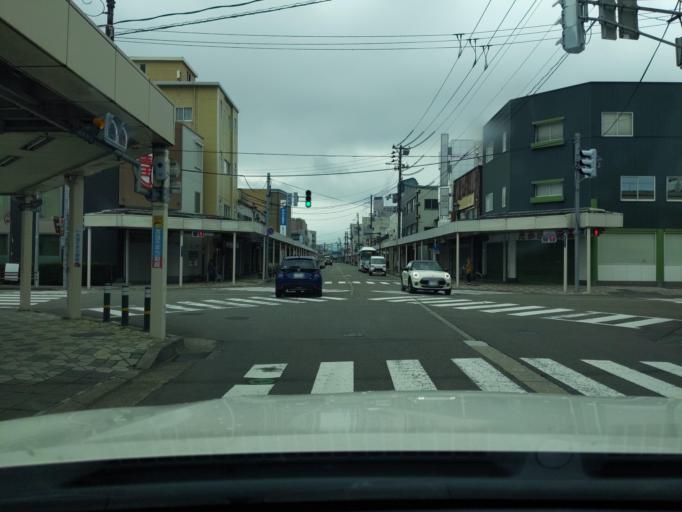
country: JP
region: Niigata
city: Kashiwazaki
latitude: 37.3678
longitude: 138.5537
